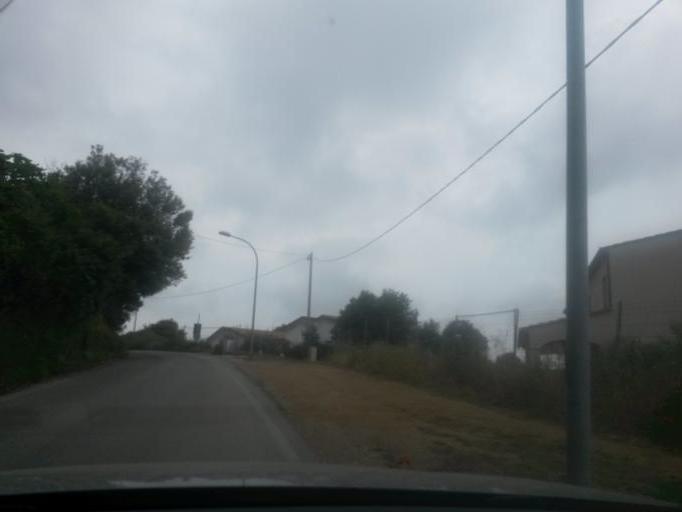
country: IT
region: Tuscany
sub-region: Provincia di Livorno
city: Capoliveri
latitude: 42.7437
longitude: 10.3853
